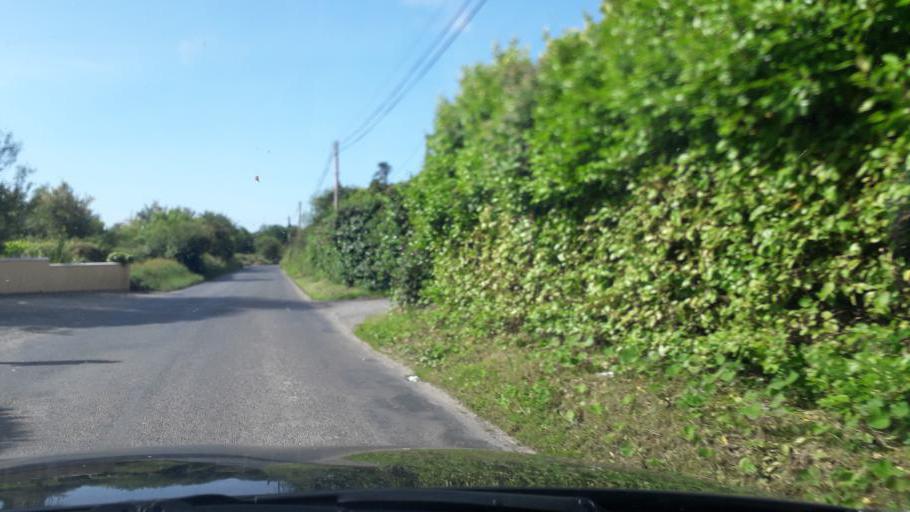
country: IE
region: Leinster
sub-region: Loch Garman
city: Loch Garman
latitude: 52.2422
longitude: -6.5501
